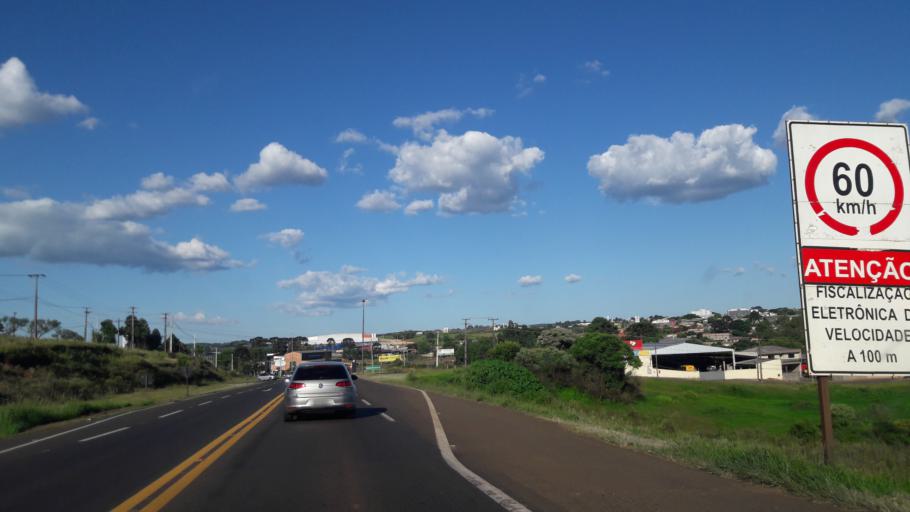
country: BR
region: Parana
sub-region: Guarapuava
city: Guarapuava
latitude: -25.3685
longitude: -51.4949
